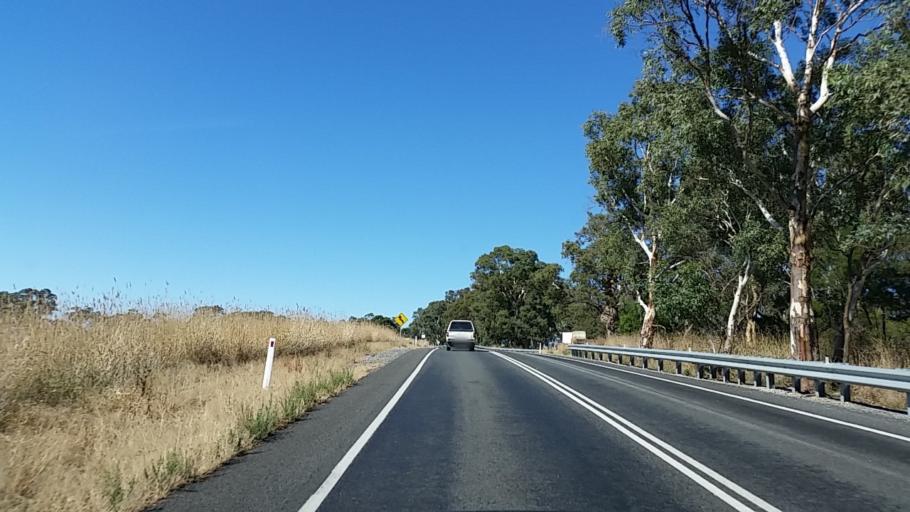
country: AU
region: South Australia
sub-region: Adelaide Hills
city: Birdwood
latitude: -34.7614
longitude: 139.0069
